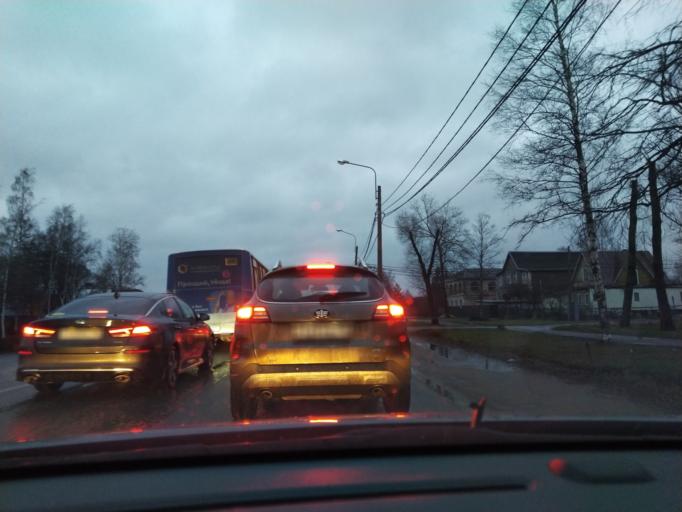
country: RU
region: St.-Petersburg
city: Uritsk
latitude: 59.8145
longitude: 30.1741
